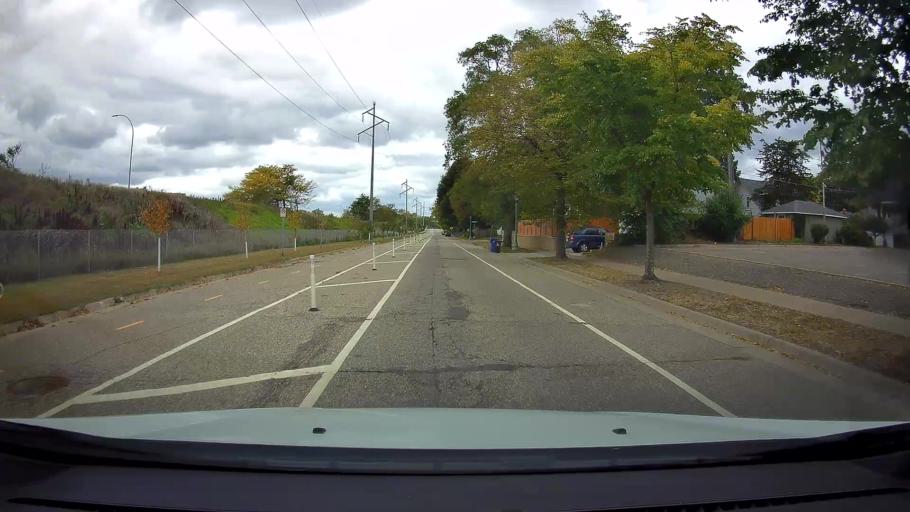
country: US
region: Minnesota
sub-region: Ramsey County
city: Falcon Heights
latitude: 44.9524
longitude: -93.1723
